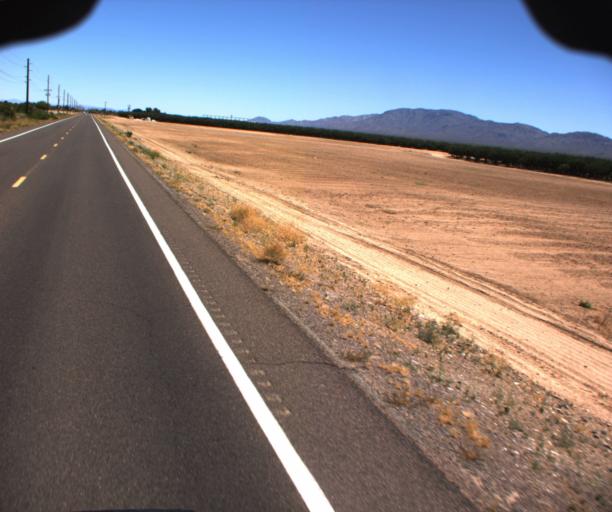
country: US
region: Arizona
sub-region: La Paz County
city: Salome
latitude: 33.8084
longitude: -113.5665
